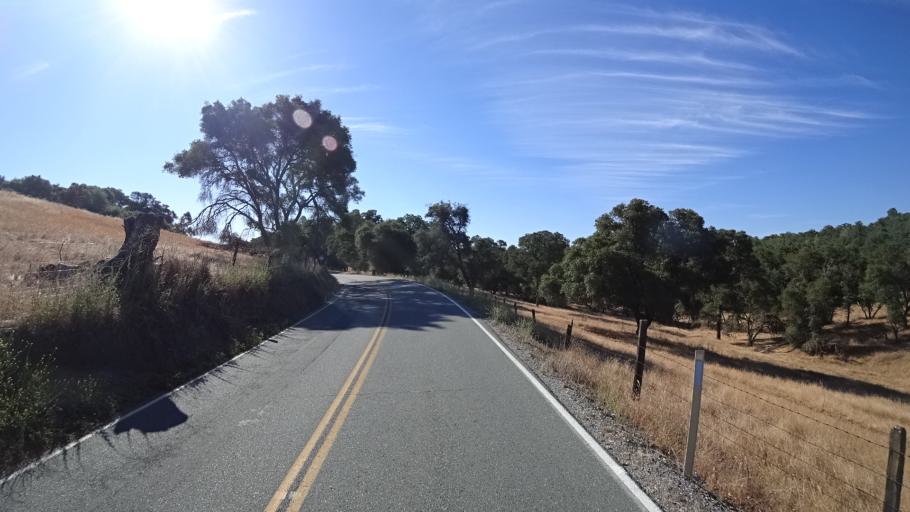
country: US
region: California
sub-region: Calaveras County
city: San Andreas
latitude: 38.1715
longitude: -120.6405
